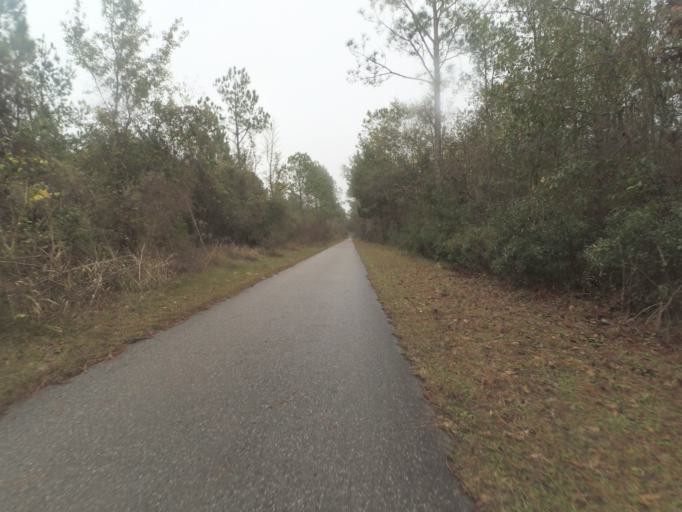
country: US
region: Florida
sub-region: Alachua County
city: Hawthorne
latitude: 29.5876
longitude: -82.1049
